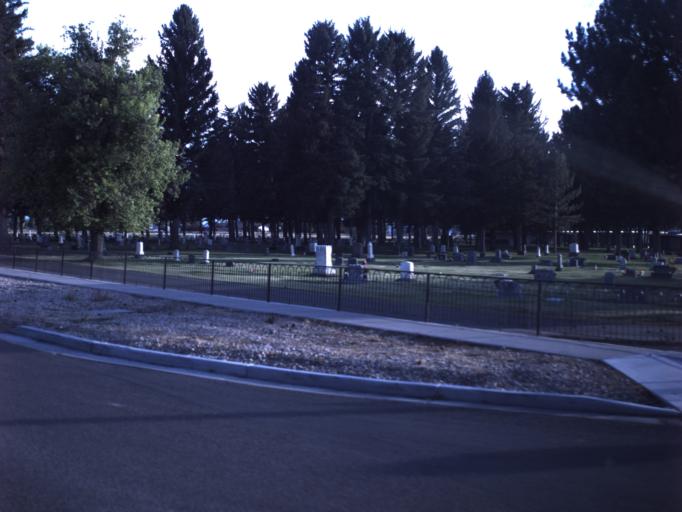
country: US
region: Utah
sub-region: Sanpete County
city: Ephraim
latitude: 39.3728
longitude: -111.5871
